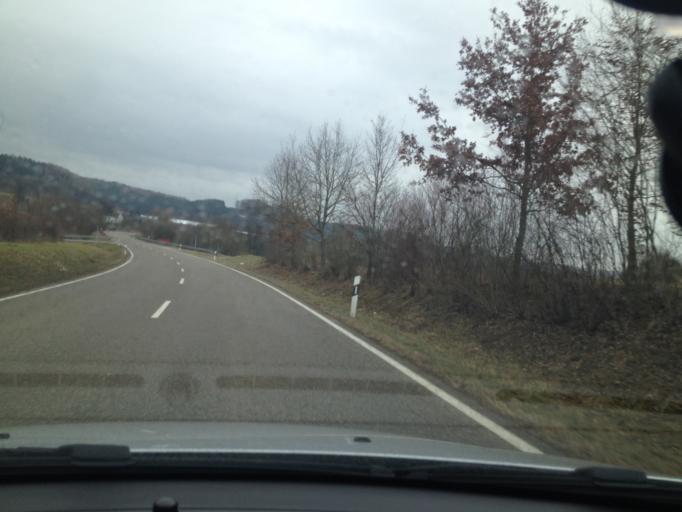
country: DE
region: Bavaria
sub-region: Swabia
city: Altenmunster
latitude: 48.4370
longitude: 10.5900
